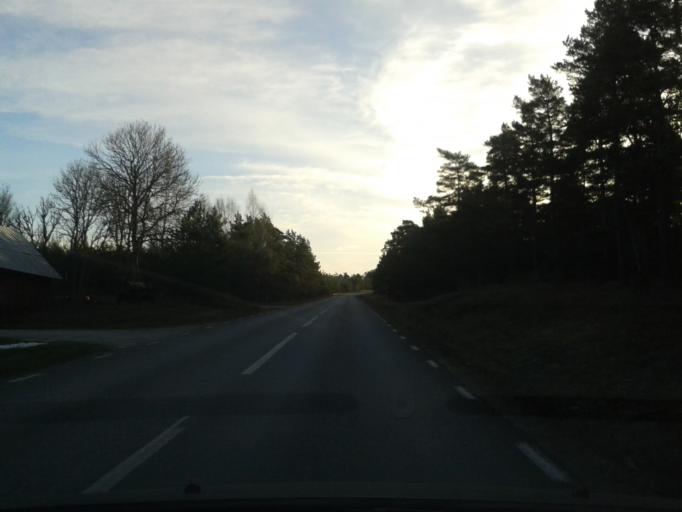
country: SE
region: Gotland
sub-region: Gotland
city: Hemse
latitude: 57.4104
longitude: 18.6334
